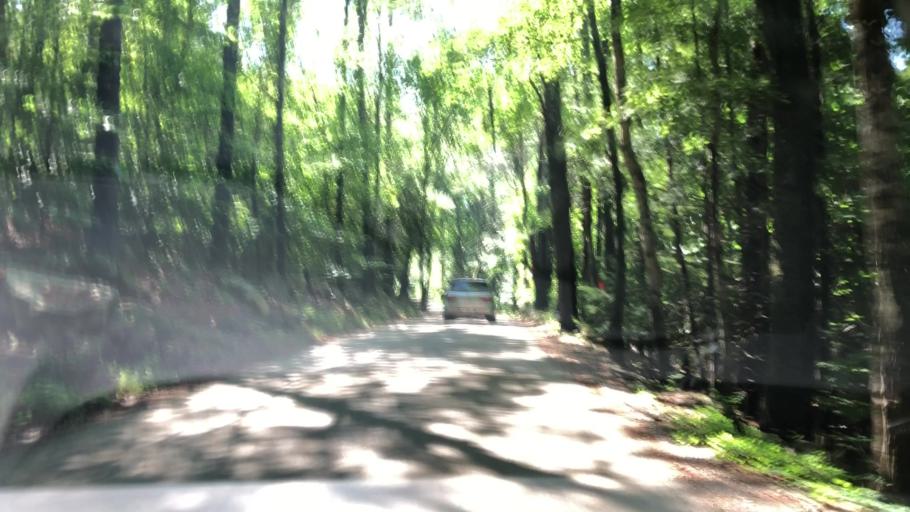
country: US
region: New Hampshire
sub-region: Hillsborough County
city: Mont Vernon
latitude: 42.9156
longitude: -71.6128
